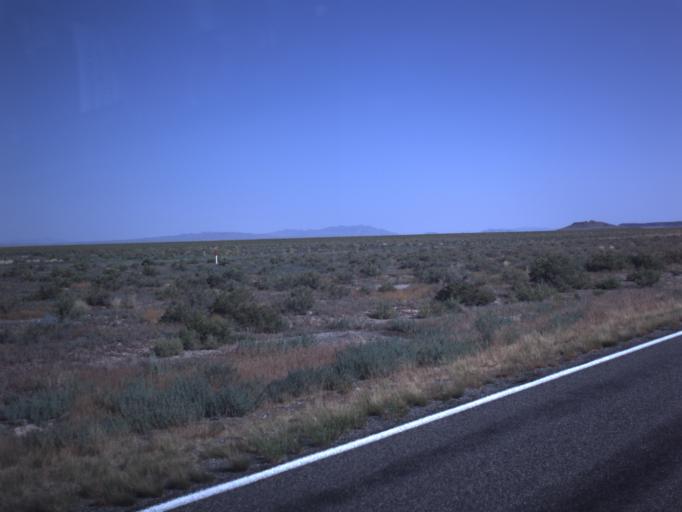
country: US
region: Utah
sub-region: Millard County
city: Delta
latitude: 39.0544
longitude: -112.7658
